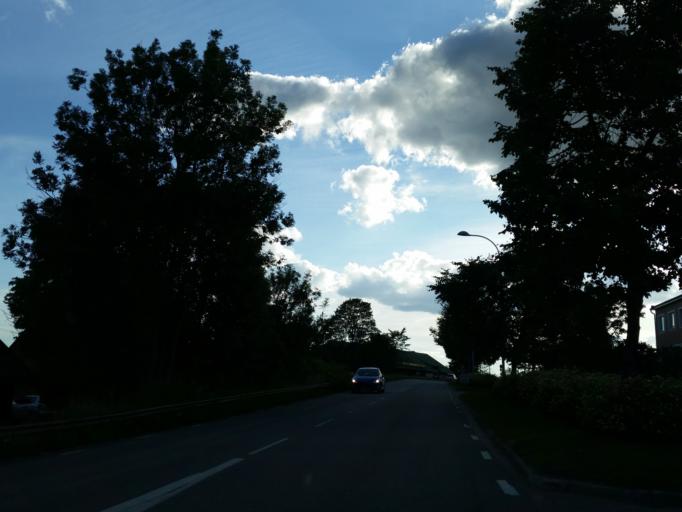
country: SE
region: Soedermanland
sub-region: Trosa Kommun
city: Vagnharad
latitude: 58.9457
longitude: 17.4958
